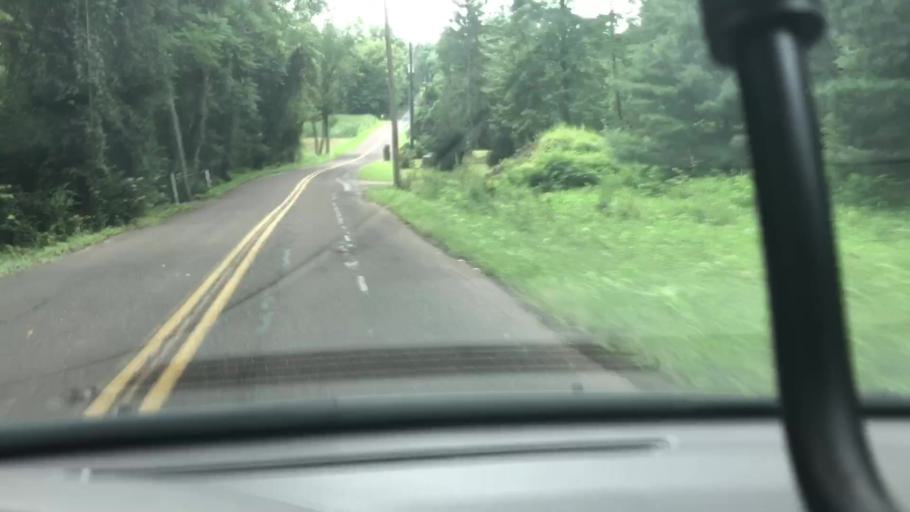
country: US
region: Pennsylvania
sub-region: Chester County
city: Kenilworth
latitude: 40.1859
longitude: -75.6515
